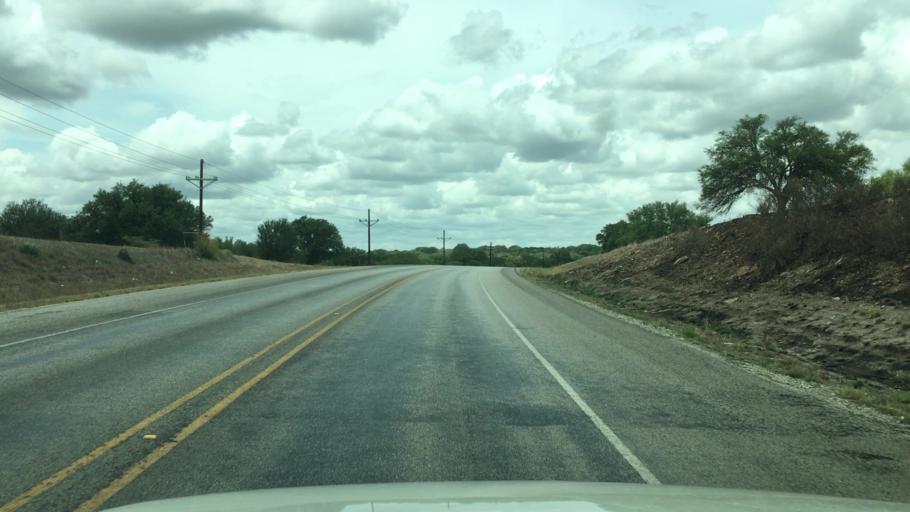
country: US
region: Texas
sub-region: McCulloch County
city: Brady
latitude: 31.0040
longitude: -99.1990
